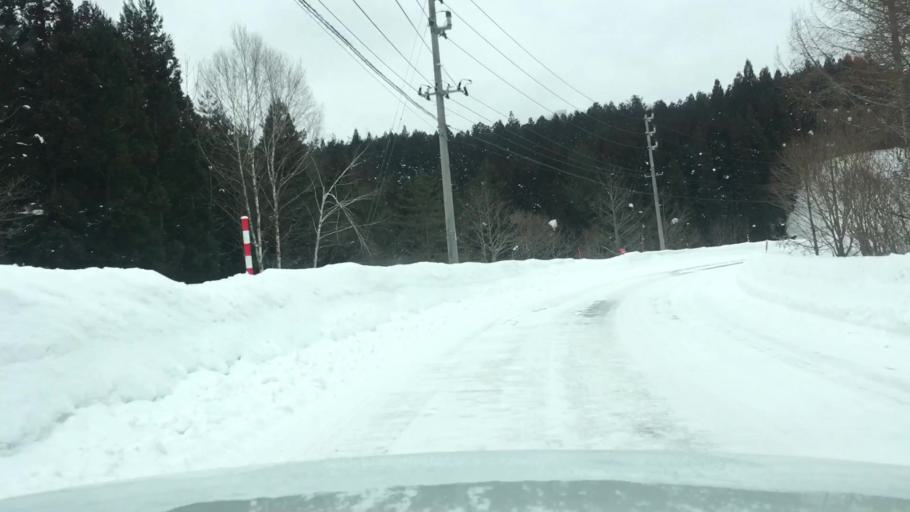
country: JP
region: Akita
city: Hanawa
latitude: 39.9951
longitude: 140.9923
